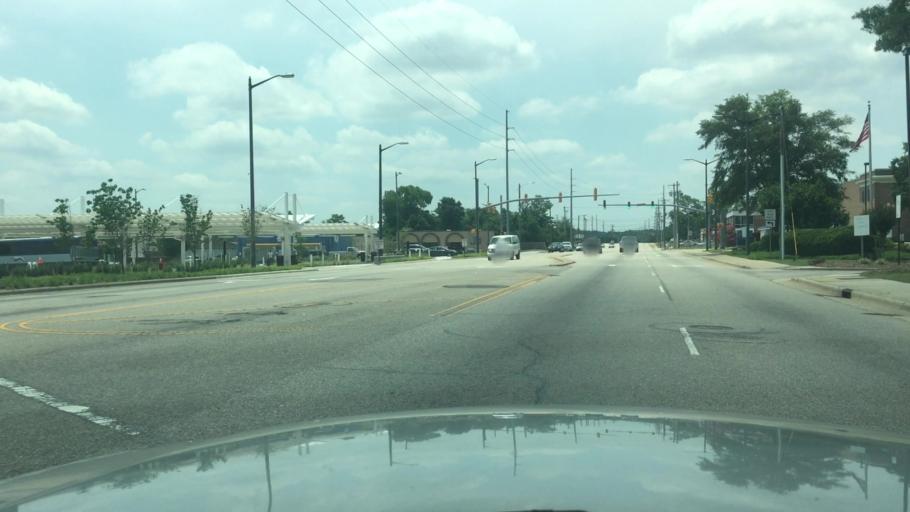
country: US
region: North Carolina
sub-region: Cumberland County
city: Fayetteville
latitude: 35.0545
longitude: -78.8873
